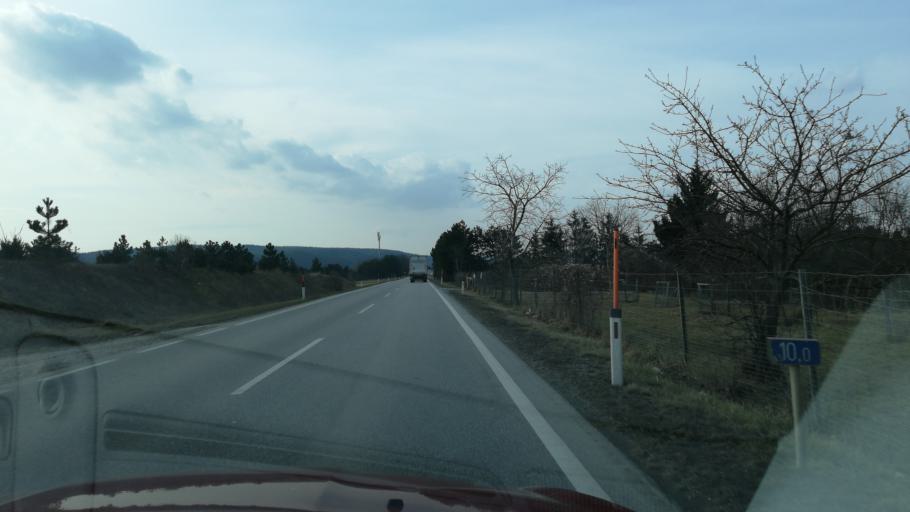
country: AT
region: Lower Austria
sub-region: Politischer Bezirk Tulln
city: Grafenworth
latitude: 48.3359
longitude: 15.8176
